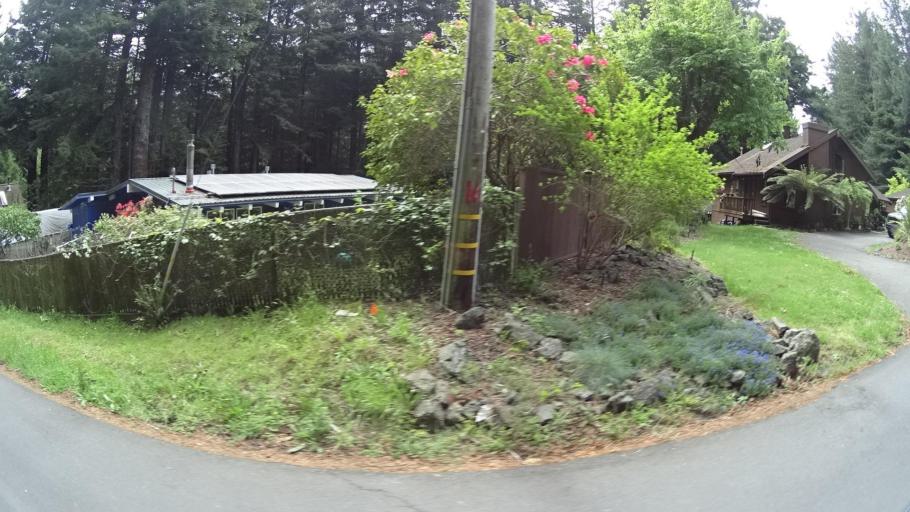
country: US
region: California
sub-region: Humboldt County
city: Bayside
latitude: 40.8494
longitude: -124.0581
